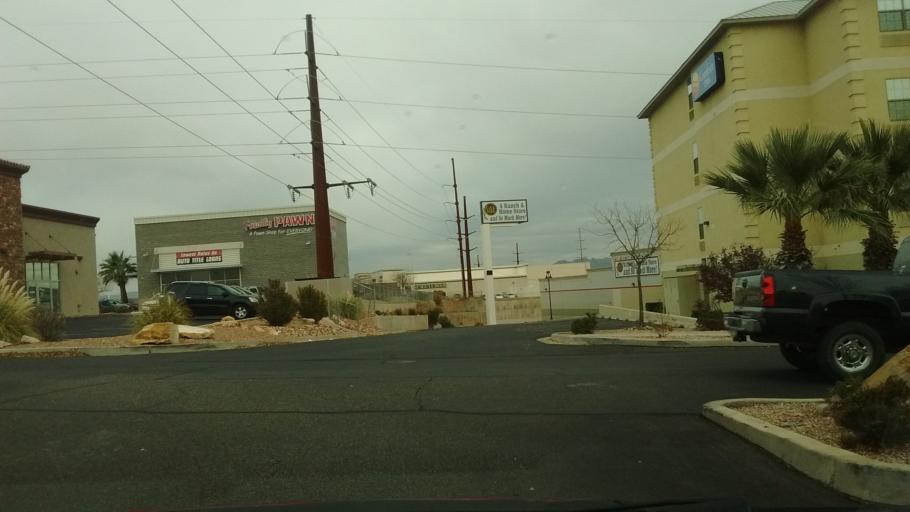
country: US
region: Utah
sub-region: Washington County
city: Washington
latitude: 37.1253
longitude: -113.5280
